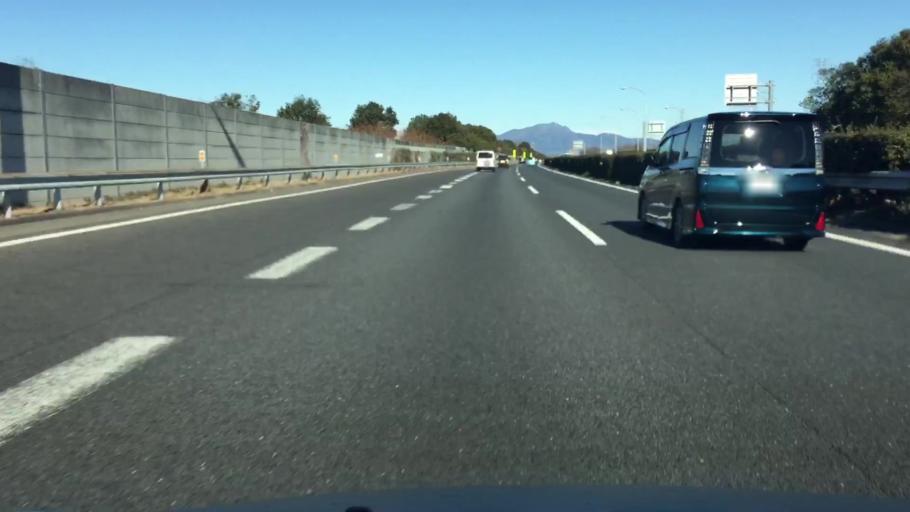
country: JP
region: Gunma
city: Maebashi-shi
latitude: 36.3753
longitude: 139.0277
